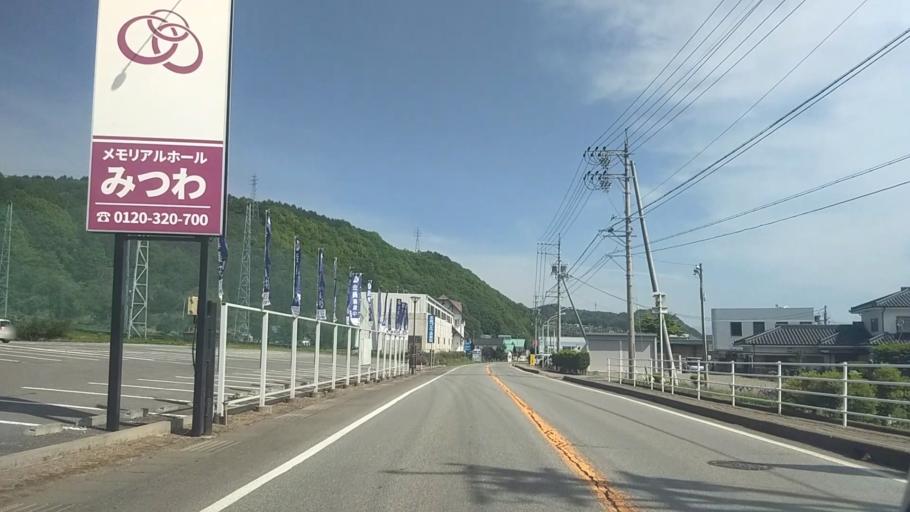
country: JP
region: Nagano
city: Saku
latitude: 36.1192
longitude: 138.4710
